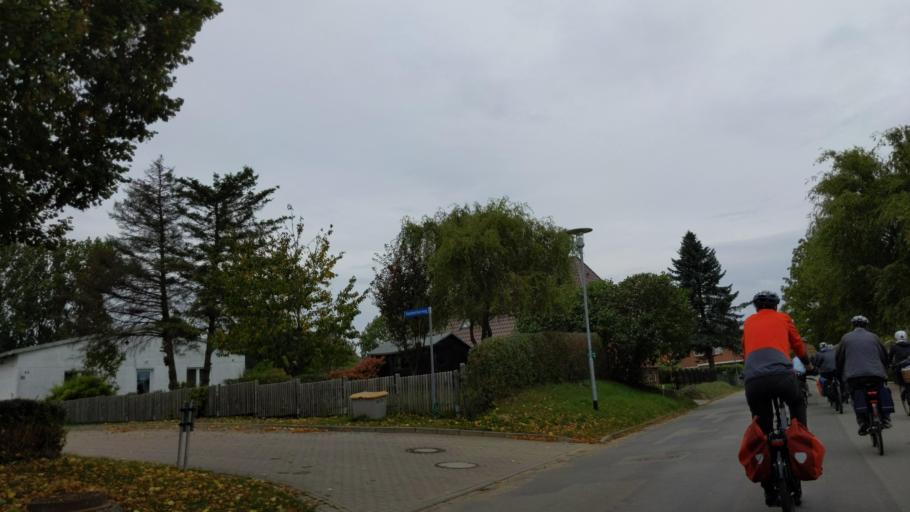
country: DE
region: Mecklenburg-Vorpommern
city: Schlagsdorf
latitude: 53.7349
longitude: 10.8257
